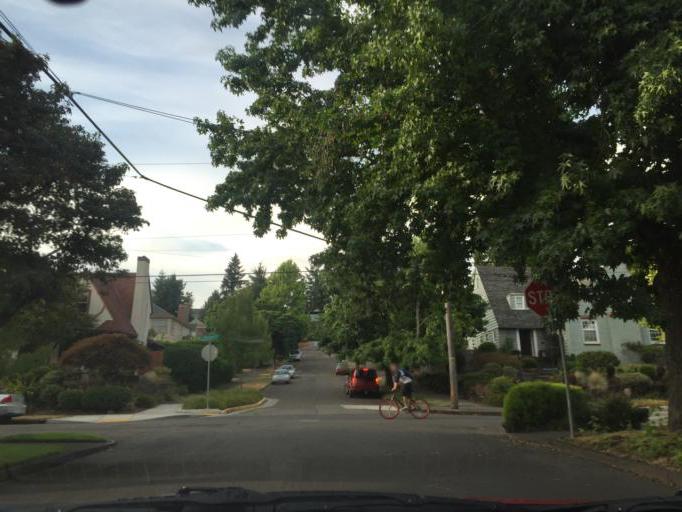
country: US
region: Oregon
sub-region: Multnomah County
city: Portland
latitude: 45.5465
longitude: -122.6327
